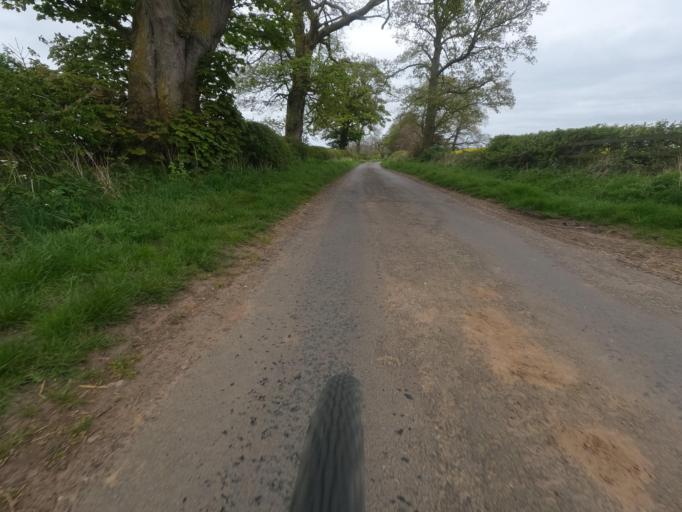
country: GB
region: England
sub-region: Northumberland
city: Meldon
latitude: 55.0692
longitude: -1.8281
